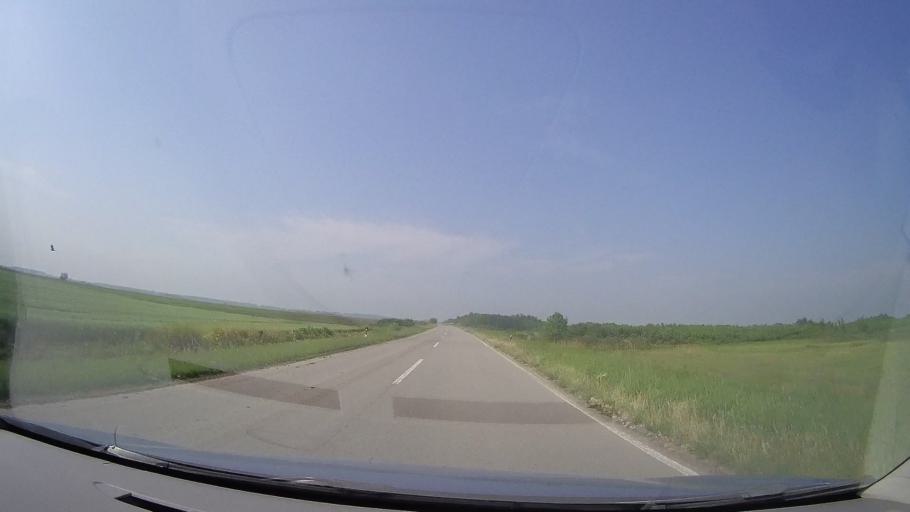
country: RS
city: Boka
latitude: 45.3984
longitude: 20.8112
